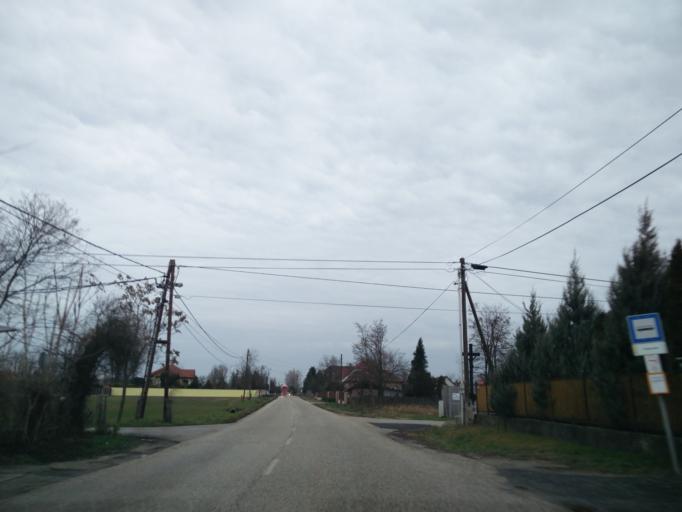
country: HU
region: Pest
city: Koka
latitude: 47.4772
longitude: 19.5682
